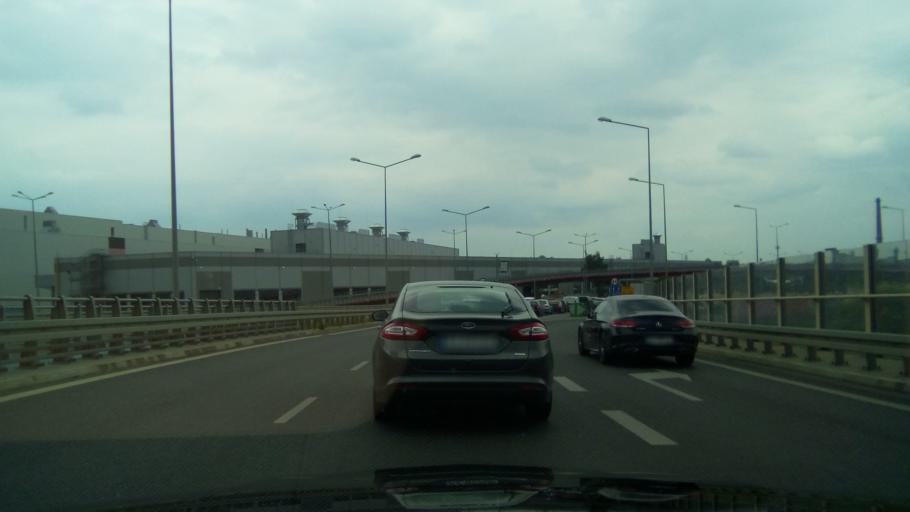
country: PL
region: Greater Poland Voivodeship
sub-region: Powiat poznanski
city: Swarzedz
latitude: 52.4115
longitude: 17.0249
